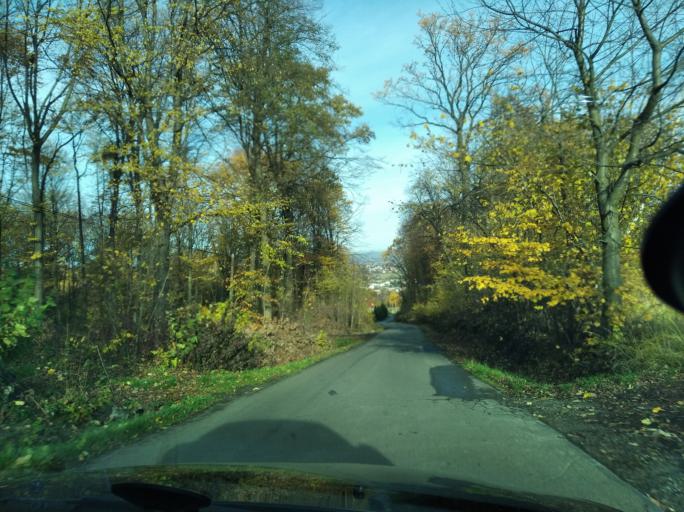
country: PL
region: Subcarpathian Voivodeship
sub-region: Powiat rzeszowski
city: Krasne
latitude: 50.0203
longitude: 22.1061
